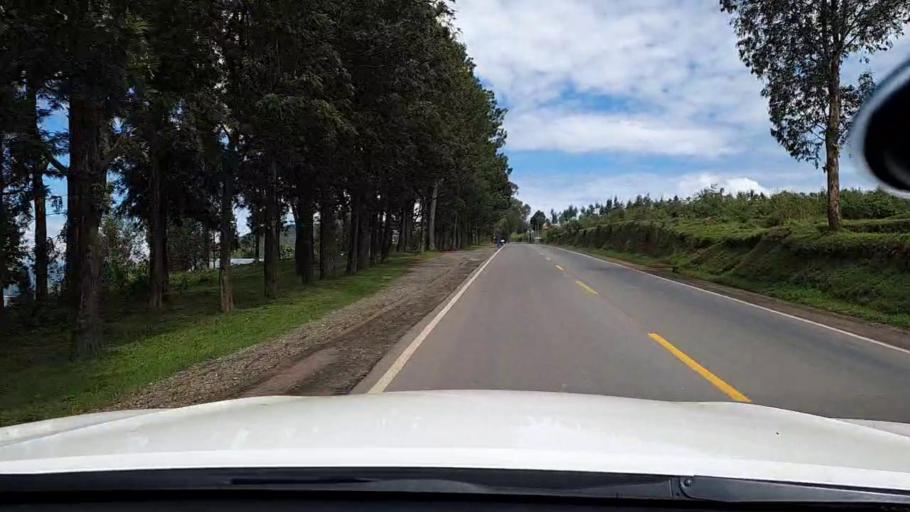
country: RW
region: Kigali
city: Kigali
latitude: -1.8415
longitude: 29.9550
